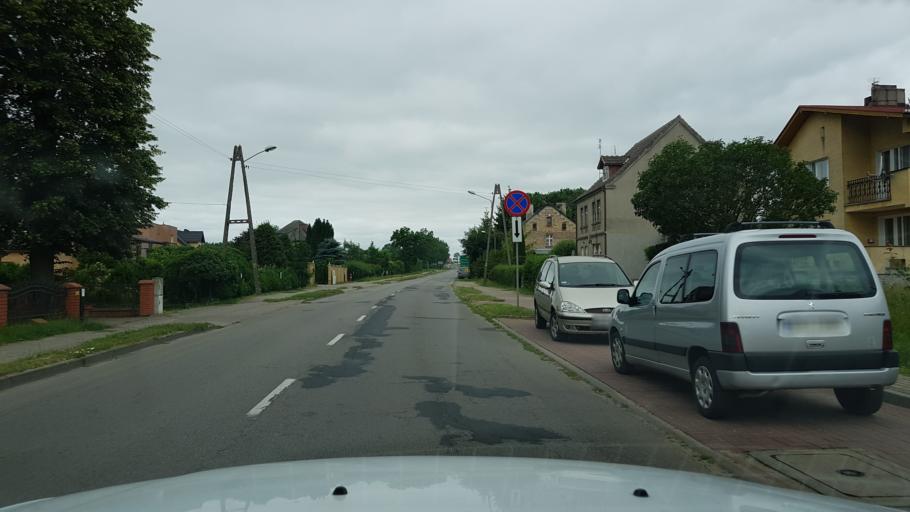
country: PL
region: West Pomeranian Voivodeship
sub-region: Powiat gryficki
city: Gryfice
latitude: 53.9086
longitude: 15.1888
